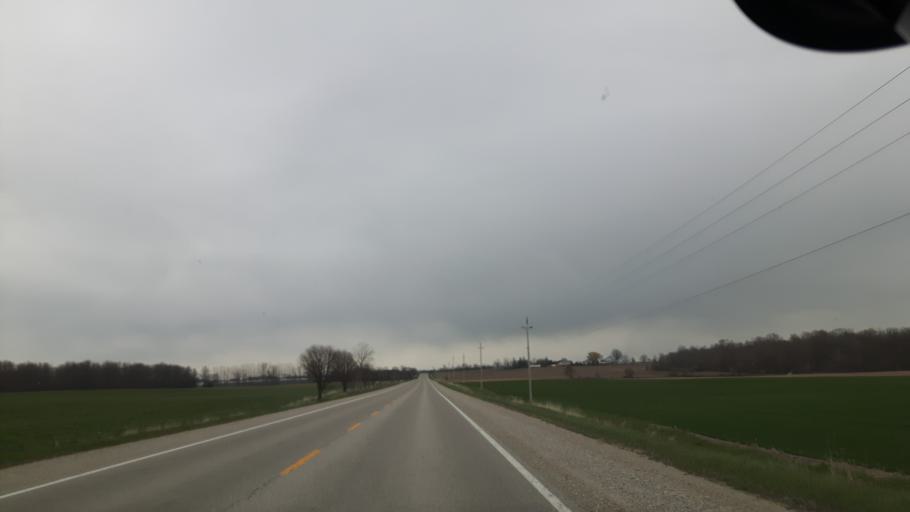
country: CA
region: Ontario
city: Bluewater
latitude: 43.5868
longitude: -81.6173
